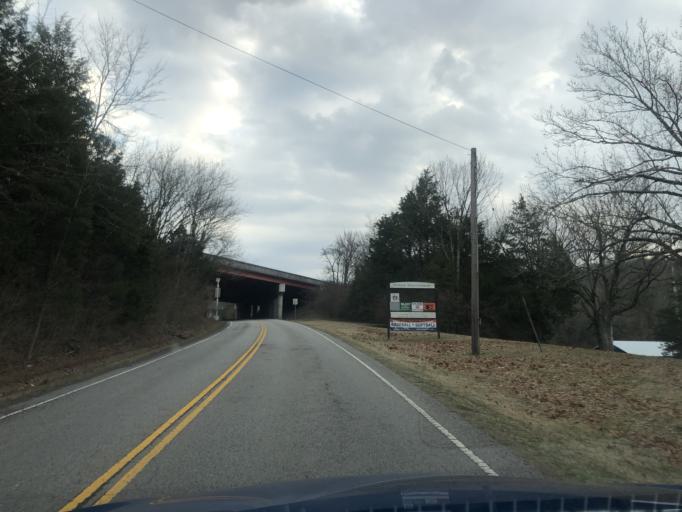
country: US
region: Tennessee
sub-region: Davidson County
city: Belle Meade
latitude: 36.1059
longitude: -86.9310
